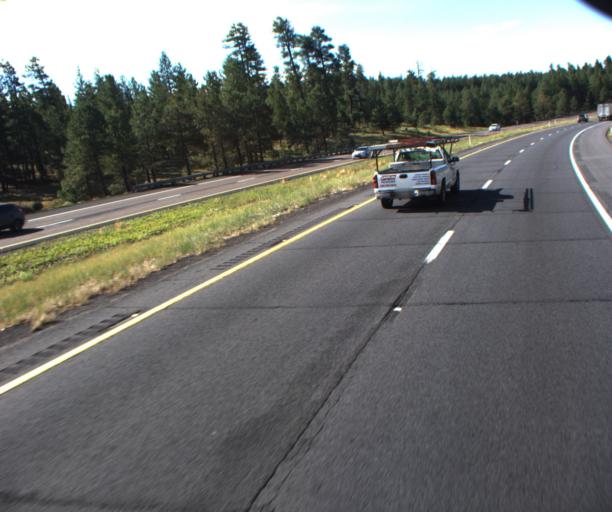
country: US
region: Arizona
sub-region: Coconino County
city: Mountainaire
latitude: 35.0712
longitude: -111.6826
